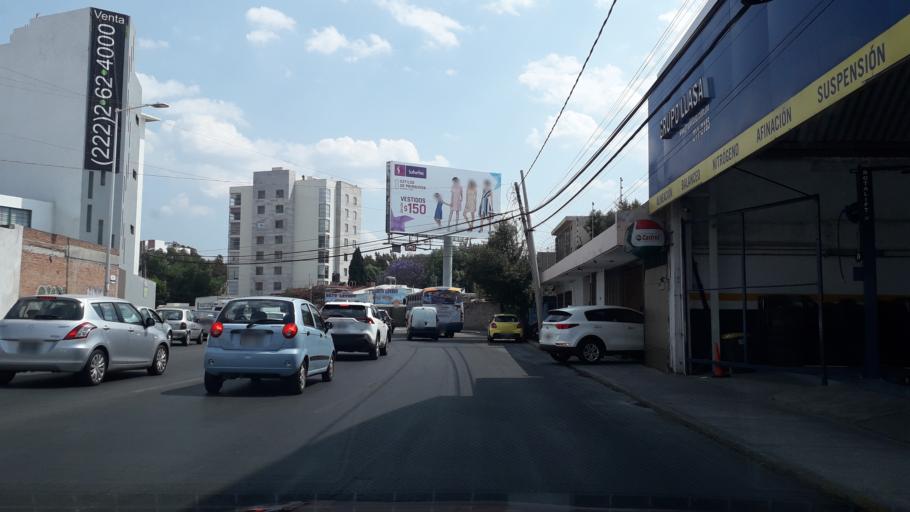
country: MX
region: Puebla
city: Puebla
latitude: 19.0293
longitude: -98.2226
